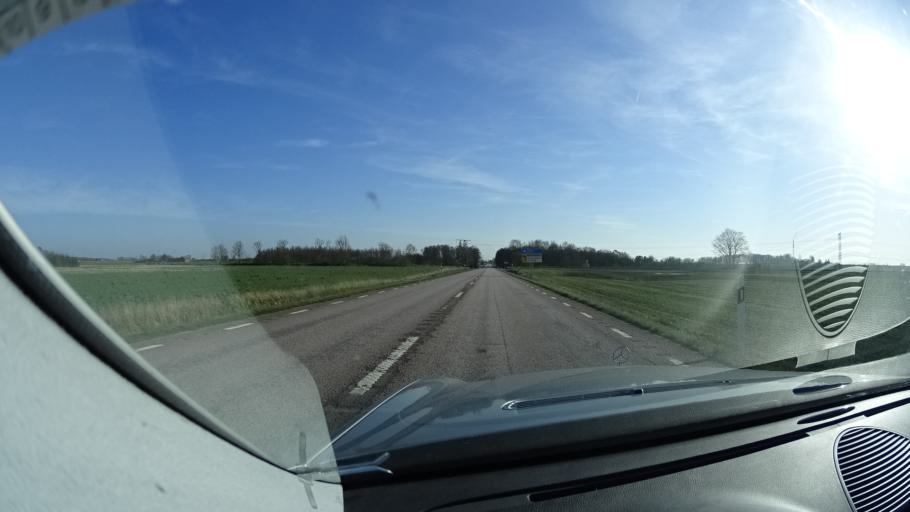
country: SE
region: Skane
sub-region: Bjuvs Kommun
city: Billesholm
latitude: 55.9929
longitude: 12.9437
